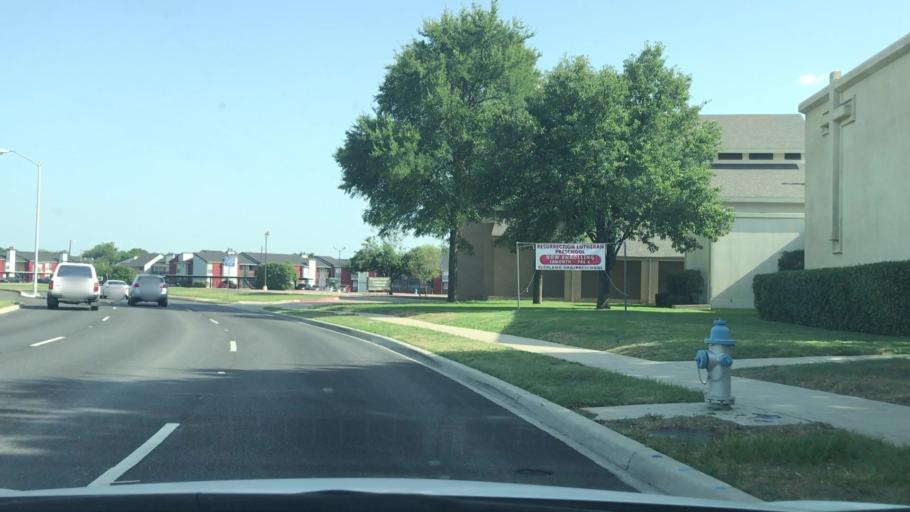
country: US
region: Texas
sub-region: Collin County
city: Plano
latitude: 33.0260
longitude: -96.7536
